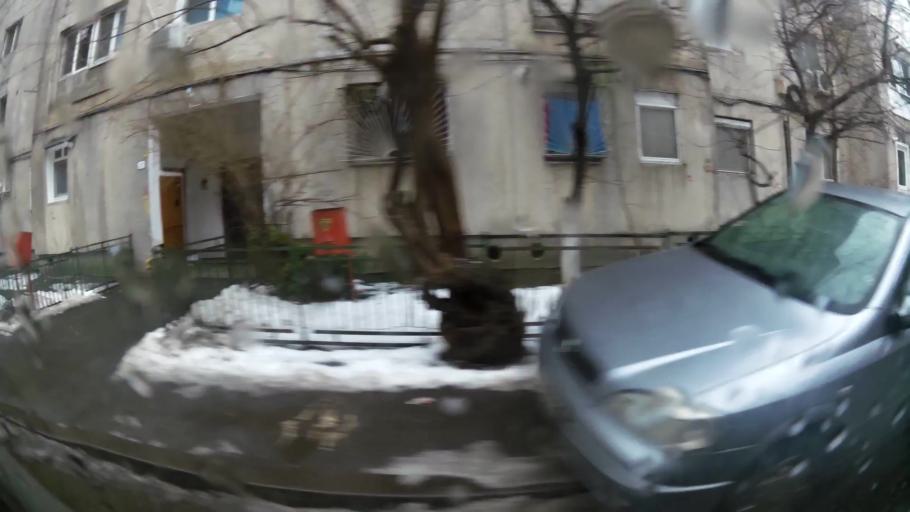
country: RO
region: Ilfov
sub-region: Comuna Chiajna
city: Rosu
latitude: 44.4310
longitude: 26.0129
